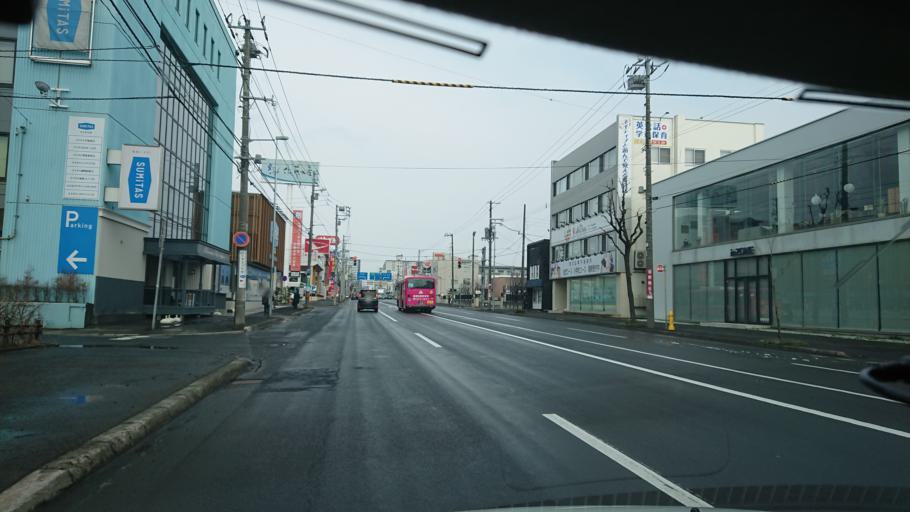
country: JP
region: Hokkaido
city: Sapporo
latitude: 43.0669
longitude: 141.3105
